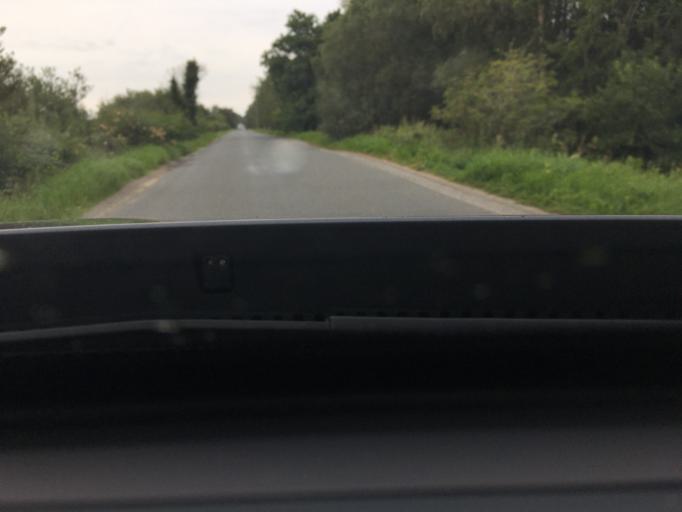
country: GB
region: Northern Ireland
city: Moy
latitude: 54.5087
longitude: -6.6364
